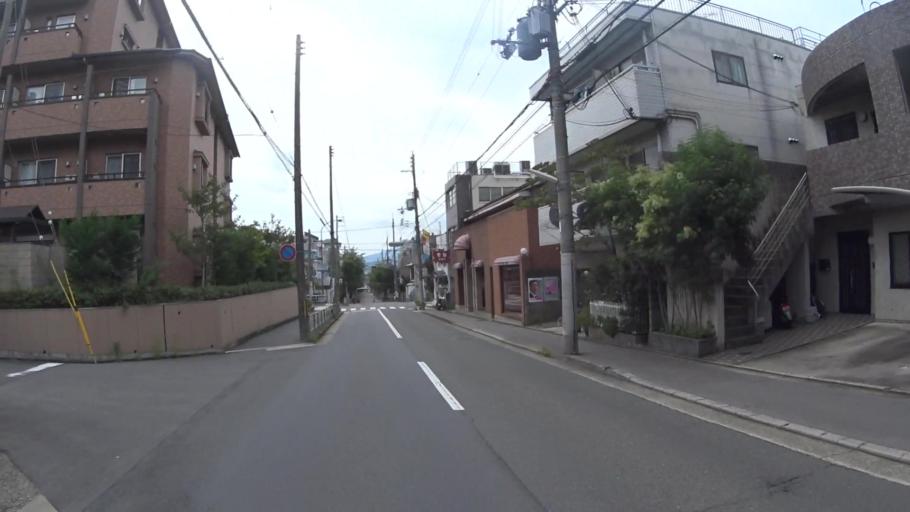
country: JP
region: Kyoto
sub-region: Kyoto-shi
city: Kamigyo-ku
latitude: 35.0330
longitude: 135.7895
